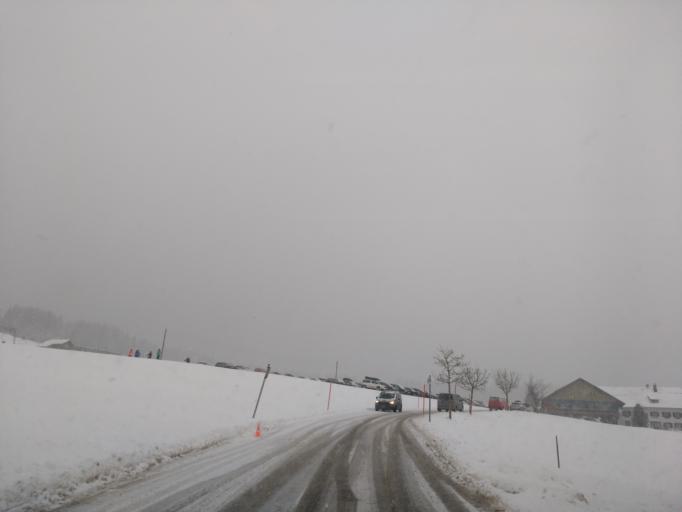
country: DE
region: Bavaria
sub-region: Swabia
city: Buchenberg
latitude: 47.7066
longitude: 10.2005
